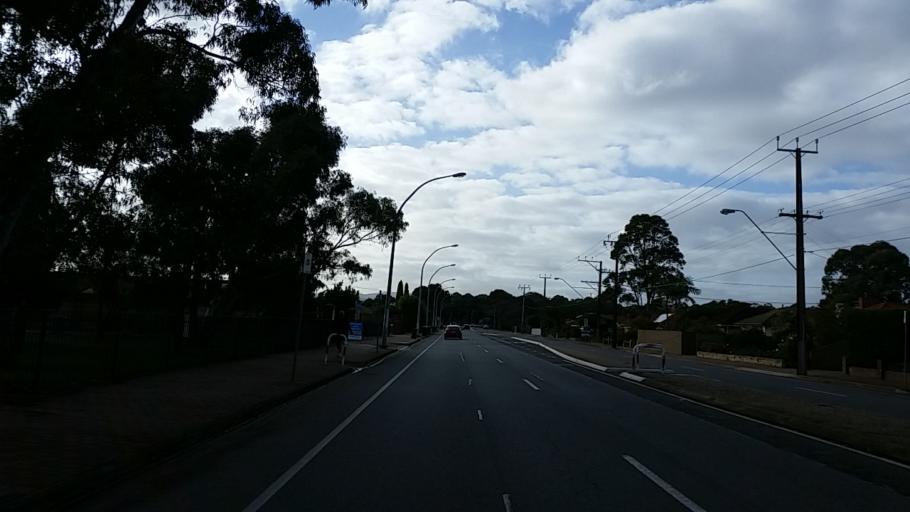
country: AU
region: South Australia
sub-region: Holdfast Bay
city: North Brighton
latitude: -34.9964
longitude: 138.5349
